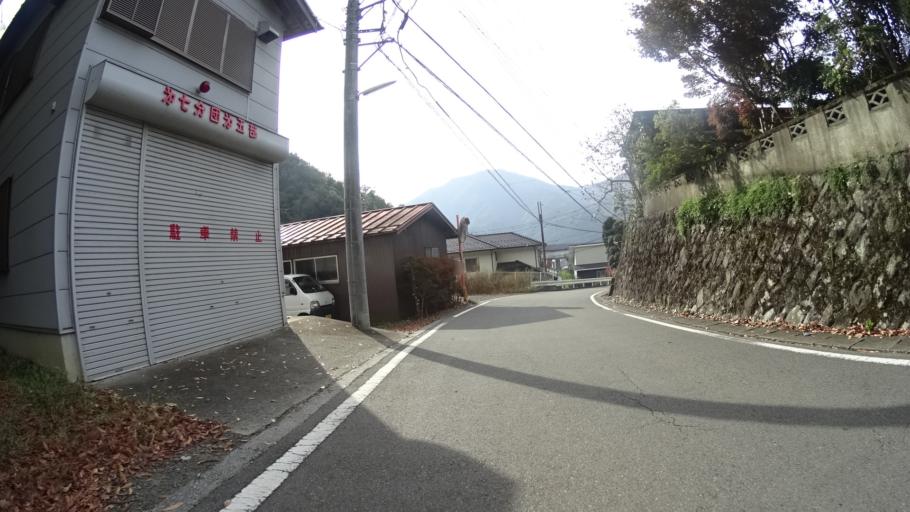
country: JP
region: Yamanashi
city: Otsuki
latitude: 35.6137
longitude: 139.0143
